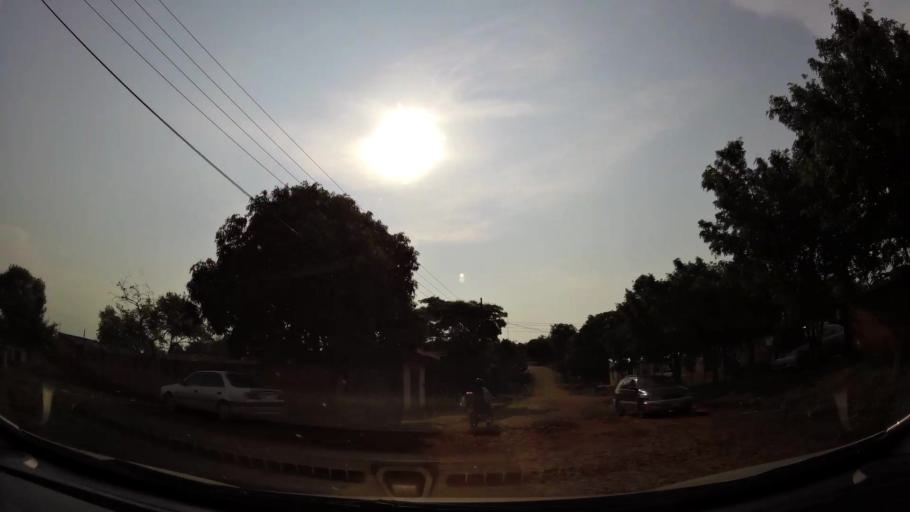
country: PY
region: Alto Parana
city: Ciudad del Este
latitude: -25.4866
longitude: -54.6575
